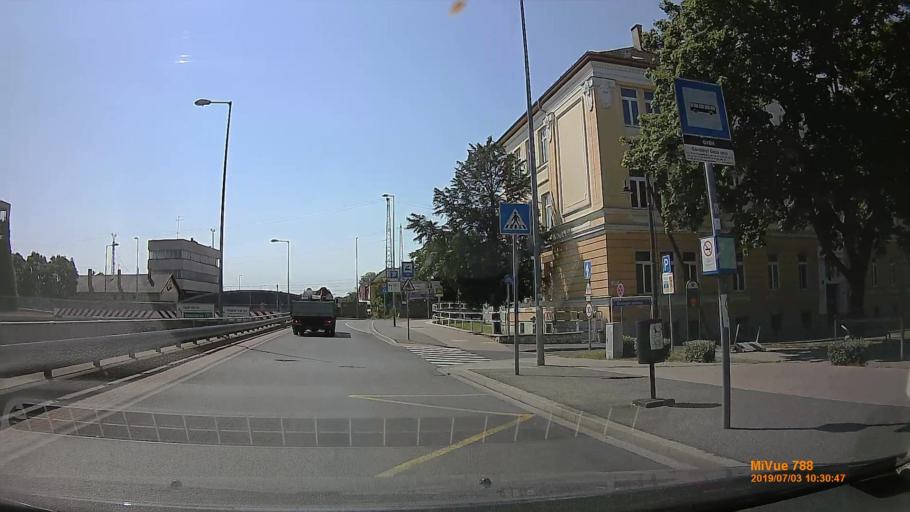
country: HU
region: Gyor-Moson-Sopron
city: Gyor
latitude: 47.6852
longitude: 17.6410
